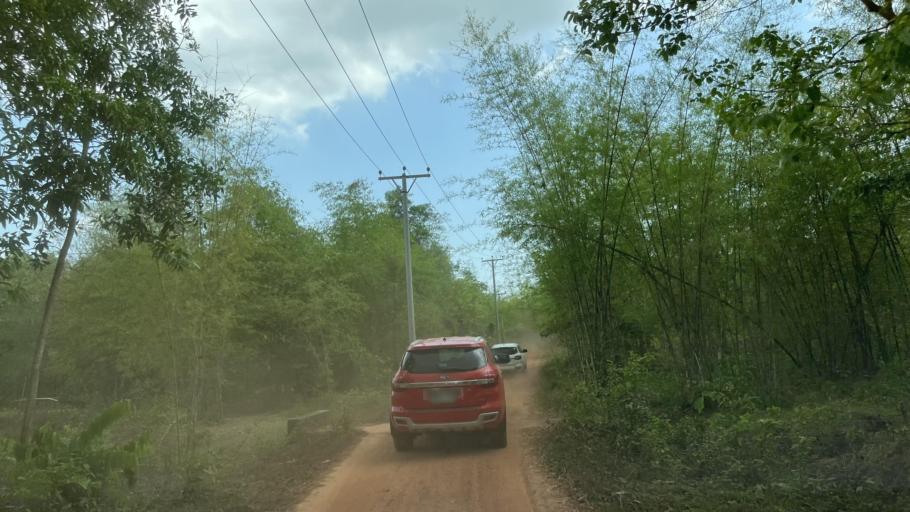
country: MM
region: Yangon
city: Twante
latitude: 16.5703
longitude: 95.9274
